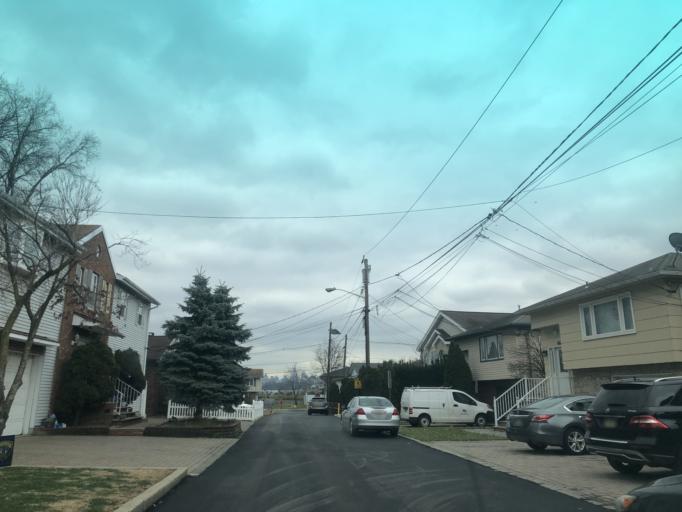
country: US
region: New Jersey
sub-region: Hudson County
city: Secaucus
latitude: 40.7986
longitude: -74.0514
